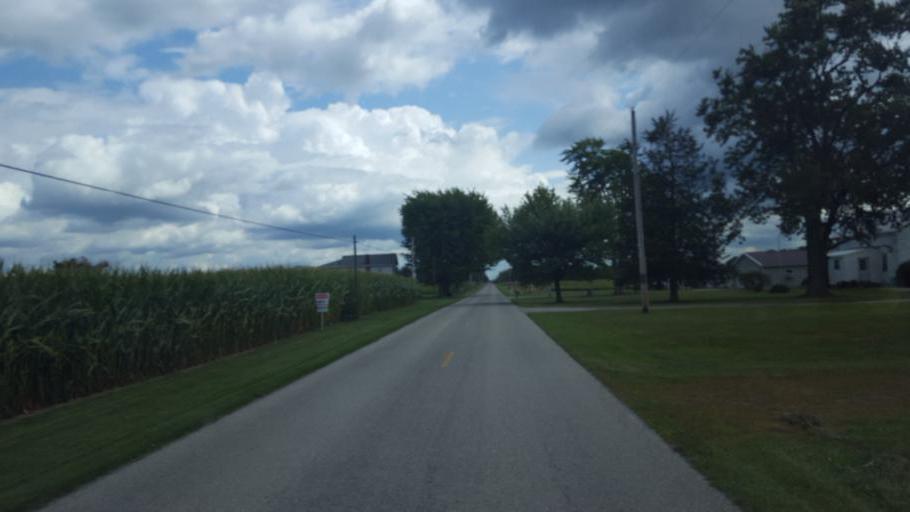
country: US
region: Ohio
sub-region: Huron County
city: Willard
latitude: 41.0954
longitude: -82.8948
